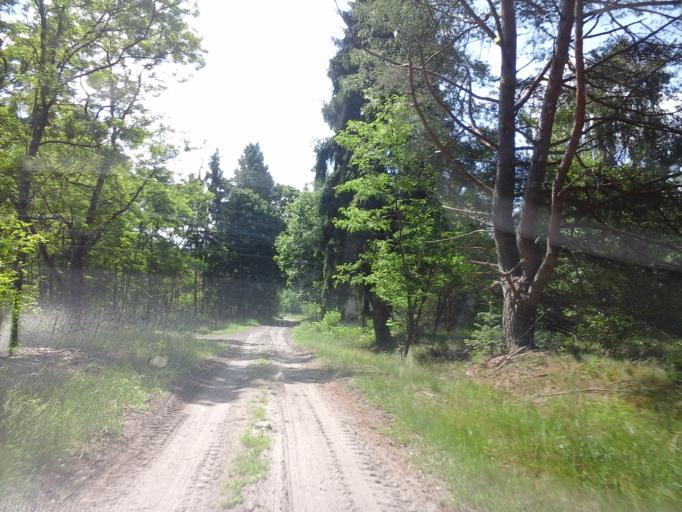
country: PL
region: West Pomeranian Voivodeship
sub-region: Powiat choszczenski
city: Bierzwnik
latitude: 53.0891
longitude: 15.7154
